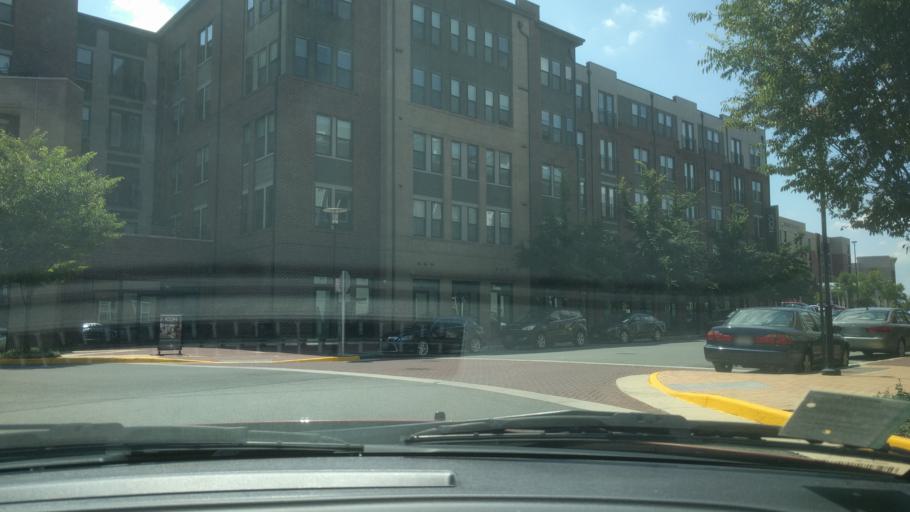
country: US
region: Virginia
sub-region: Fairfax County
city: Floris
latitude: 38.9570
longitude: -77.4184
